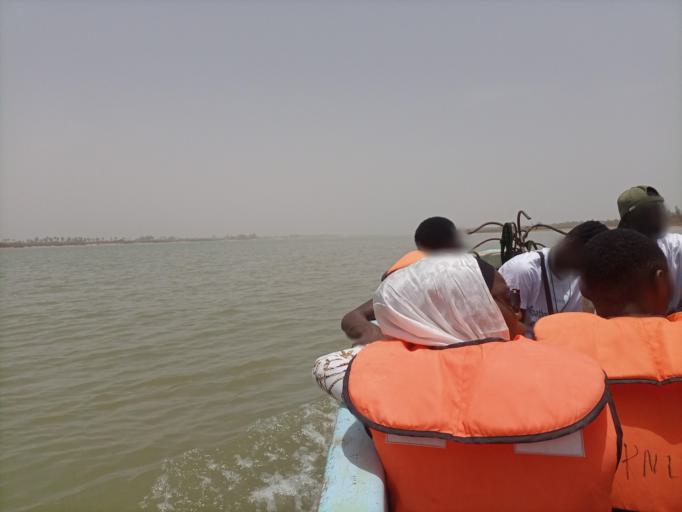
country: SN
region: Saint-Louis
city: Saint-Louis
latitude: 15.8557
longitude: -16.5176
